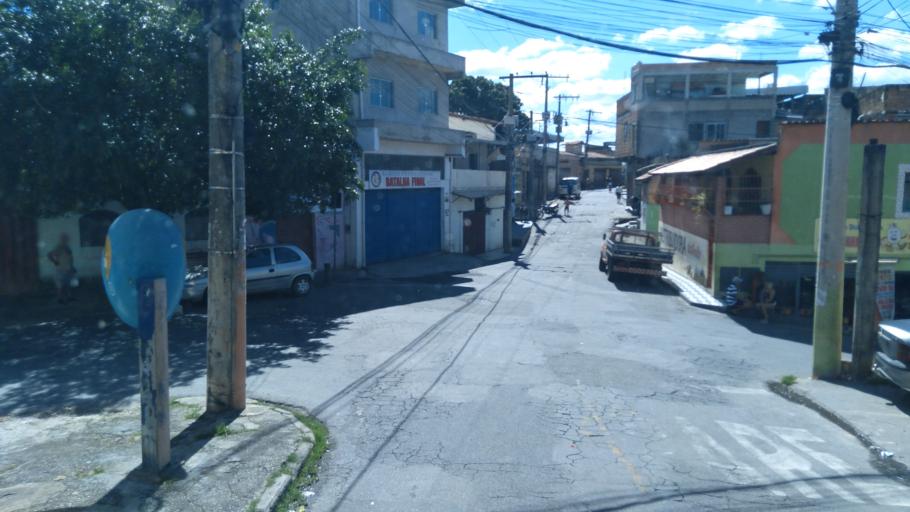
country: BR
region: Minas Gerais
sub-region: Belo Horizonte
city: Belo Horizonte
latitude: -19.8535
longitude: -43.8860
